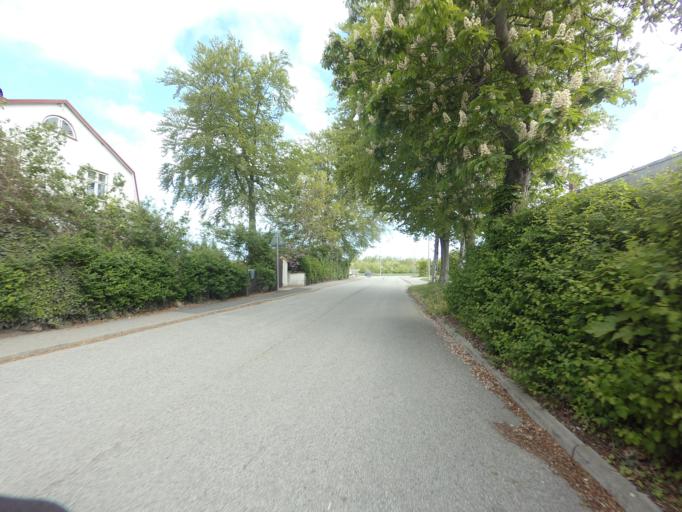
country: SE
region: Skane
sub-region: Malmo
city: Bunkeflostrand
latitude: 55.5571
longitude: 12.9637
